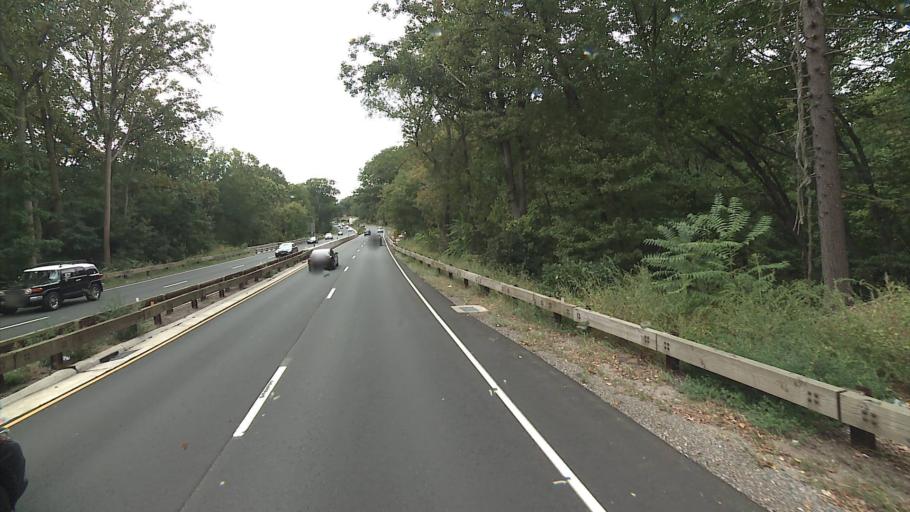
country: US
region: Connecticut
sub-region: Fairfield County
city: North Stamford
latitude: 41.1087
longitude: -73.5548
